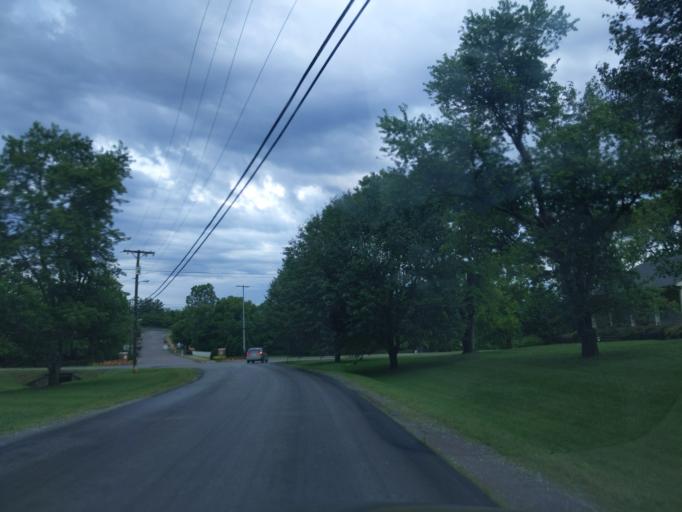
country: US
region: Tennessee
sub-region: Williamson County
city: Brentwood Estates
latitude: 36.0343
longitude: -86.7427
